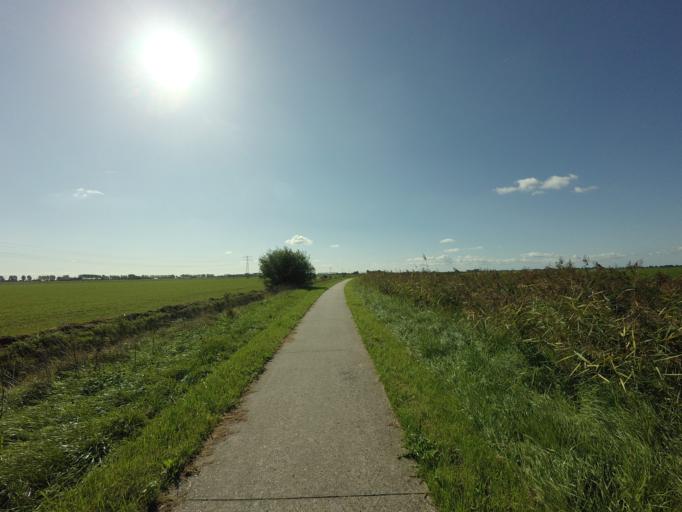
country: NL
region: Friesland
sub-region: Gemeente Boarnsterhim
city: Reduzum
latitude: 53.1449
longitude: 5.7644
